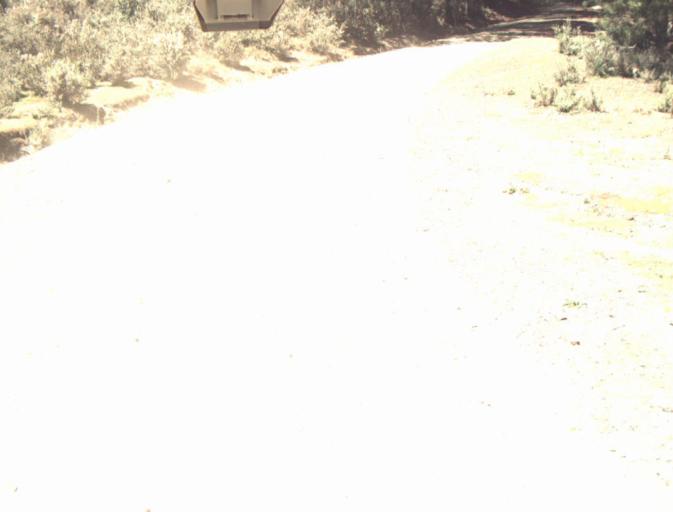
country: AU
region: Tasmania
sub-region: Dorset
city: Scottsdale
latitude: -41.3591
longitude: 147.4271
